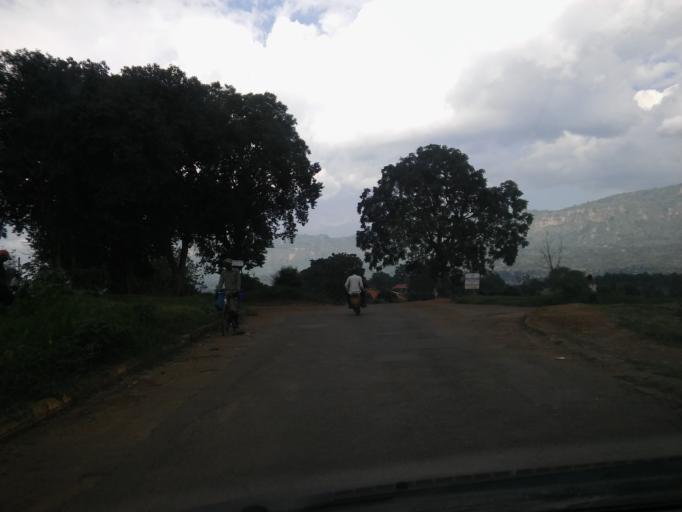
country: UG
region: Eastern Region
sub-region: Mbale District
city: Mbale
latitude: 1.0678
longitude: 34.1849
